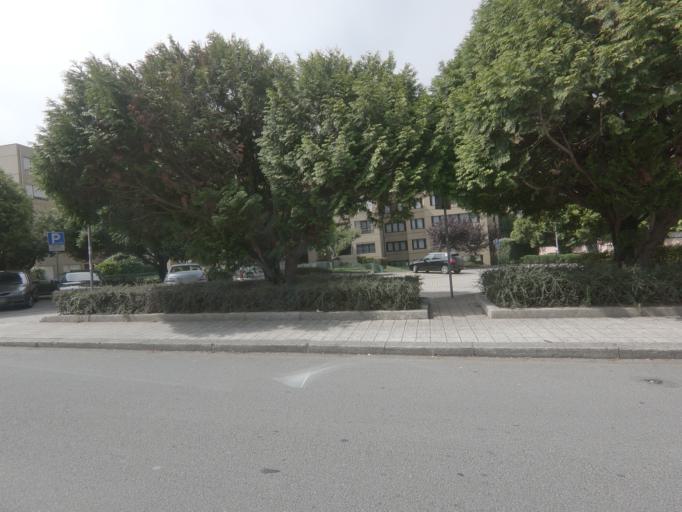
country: PT
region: Porto
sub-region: Matosinhos
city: Senhora da Hora
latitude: 41.1626
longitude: -8.6388
